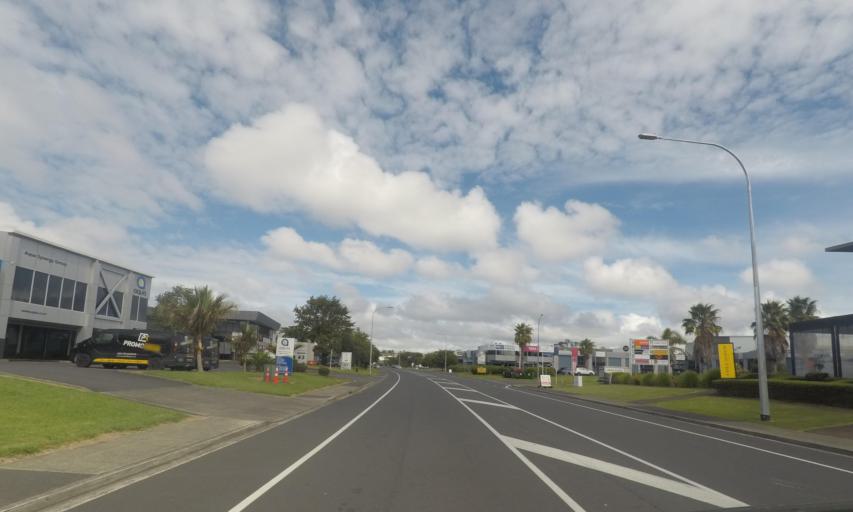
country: NZ
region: Auckland
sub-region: Auckland
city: Rothesay Bay
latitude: -36.7445
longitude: 174.6973
